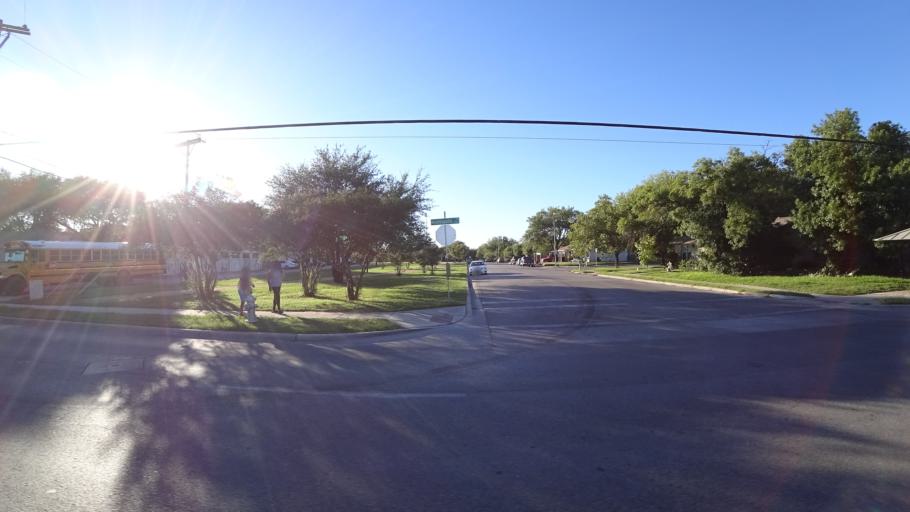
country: US
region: Texas
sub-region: Travis County
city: Austin
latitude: 30.2321
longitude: -97.6988
